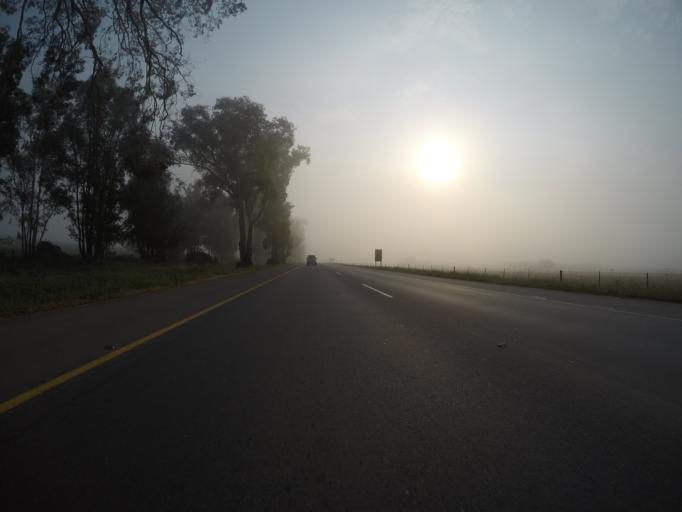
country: ZA
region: Western Cape
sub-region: City of Cape Town
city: Kraaifontein
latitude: -33.8012
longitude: 18.6851
